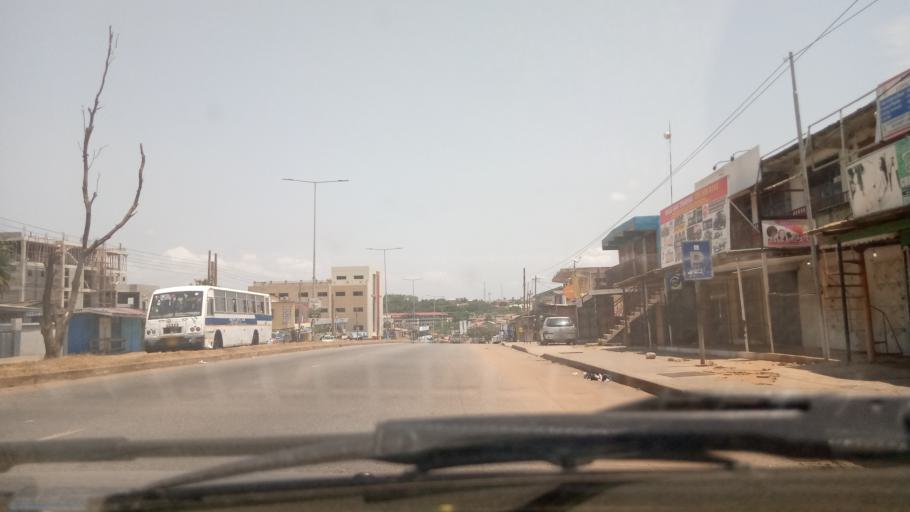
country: GH
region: Greater Accra
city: Accra
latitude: 5.5650
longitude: -0.2443
